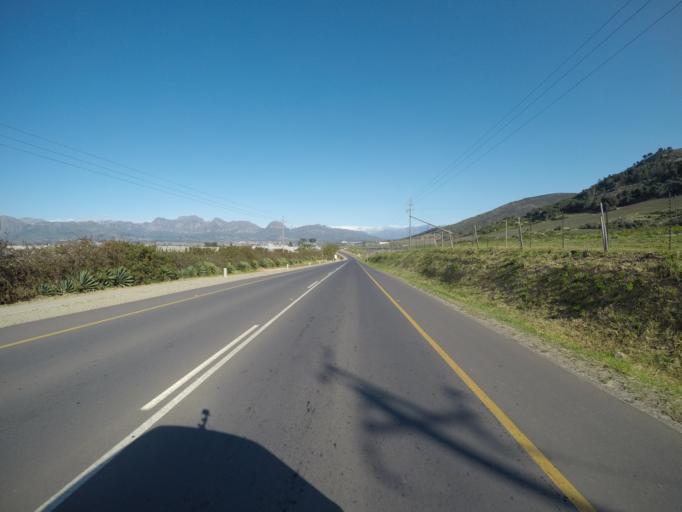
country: ZA
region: Western Cape
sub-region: Cape Winelands District Municipality
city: Noorder-Paarl
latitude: -33.6839
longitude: 18.9474
